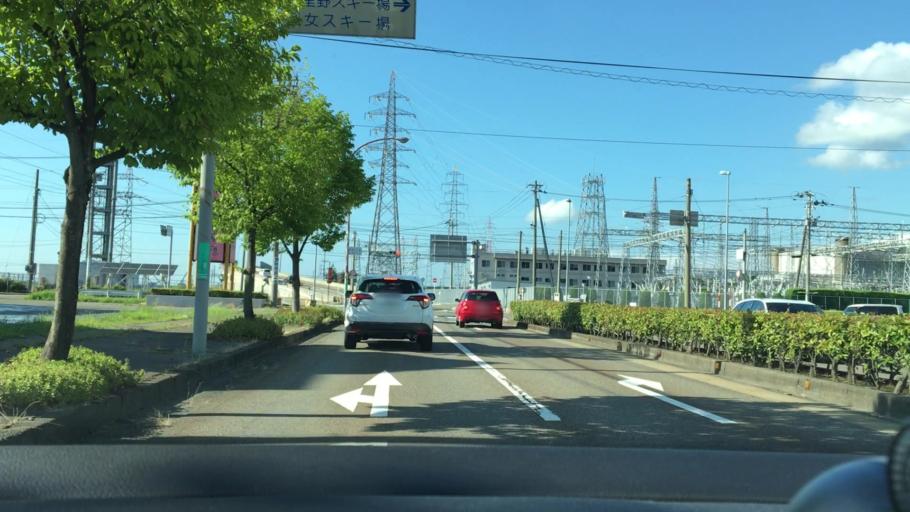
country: JP
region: Fukui
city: Fukui-shi
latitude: 36.0892
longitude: 136.2825
